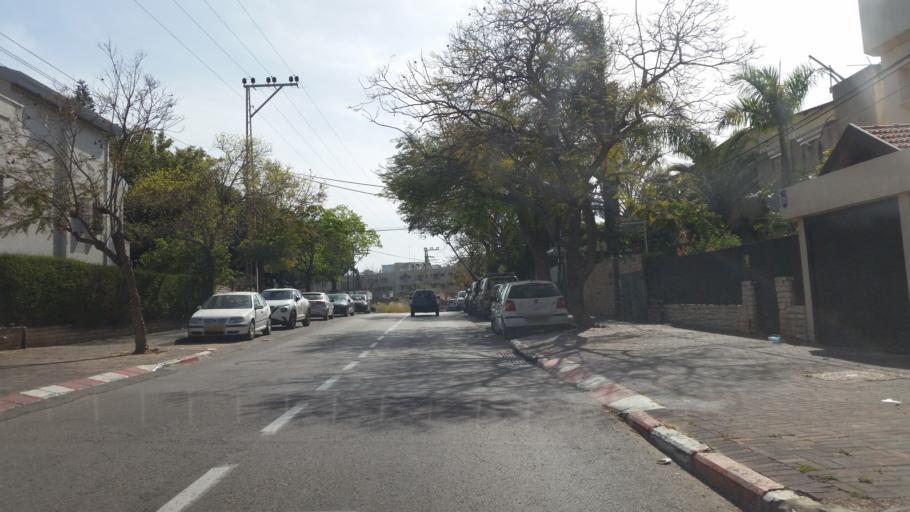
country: IL
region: Tel Aviv
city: Ramat HaSharon
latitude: 32.1578
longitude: 34.8504
